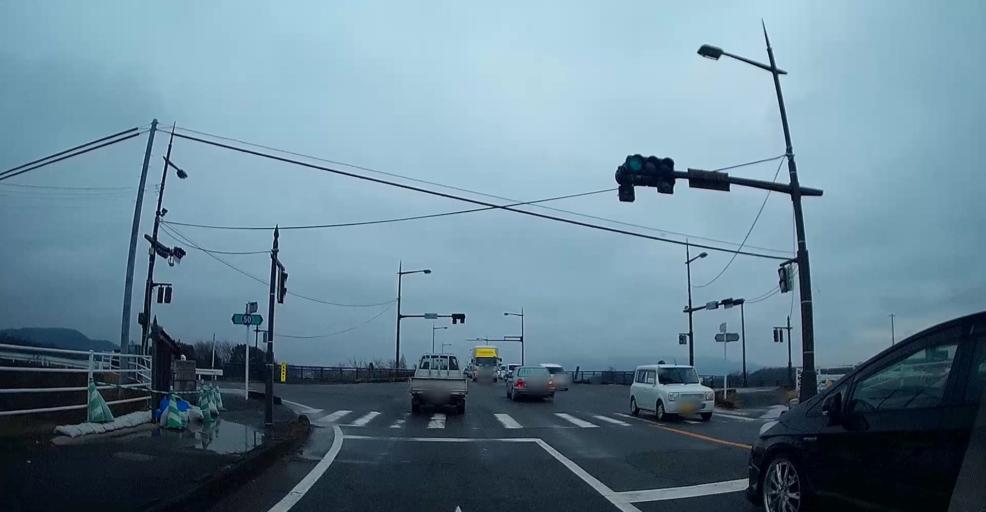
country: JP
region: Kumamoto
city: Kumamoto
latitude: 32.7381
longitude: 130.7402
